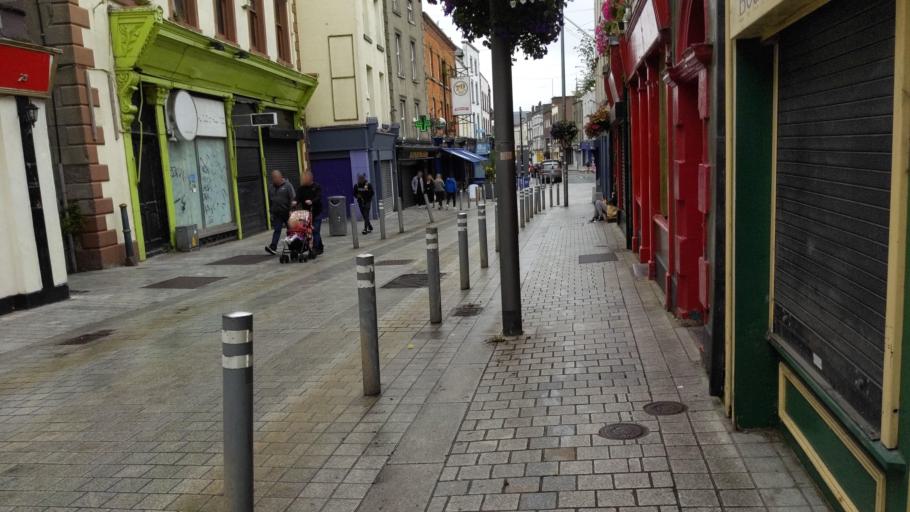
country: IE
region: Leinster
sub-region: Lu
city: Drogheda
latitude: 53.7157
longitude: -6.3559
